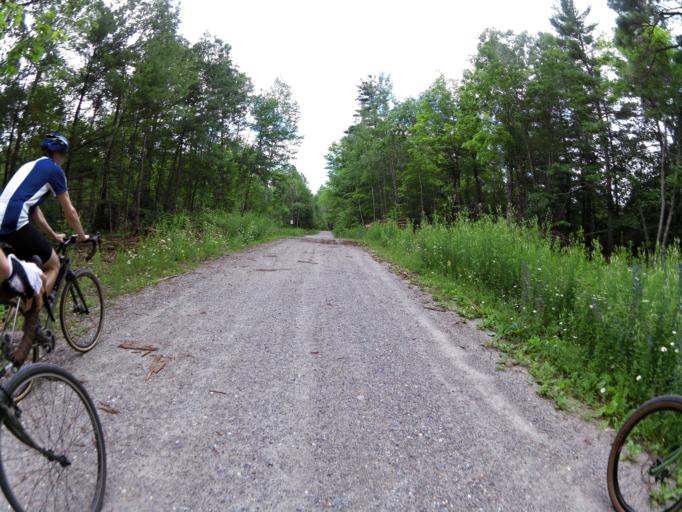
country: CA
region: Ontario
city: Perth
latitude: 45.0093
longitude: -76.5881
